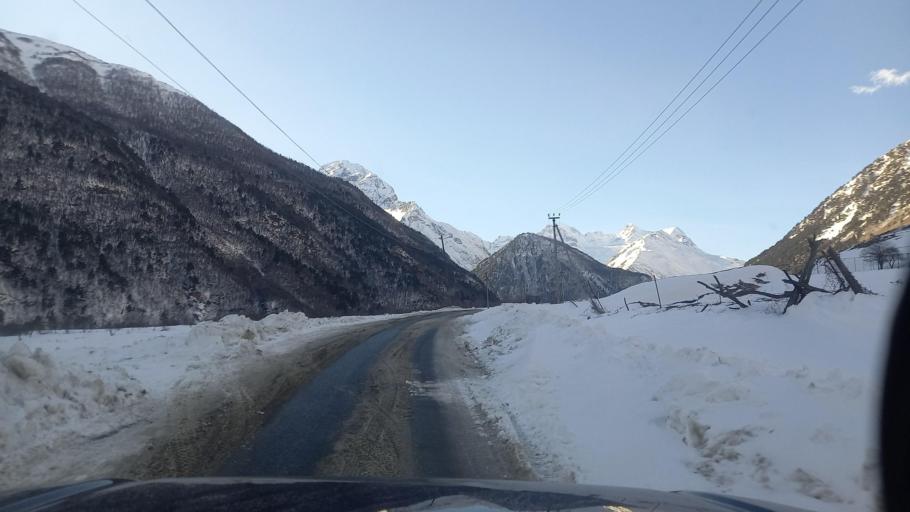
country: RU
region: Kabardino-Balkariya
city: Verkhnyaya Balkariya
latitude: 42.9020
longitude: 43.6370
